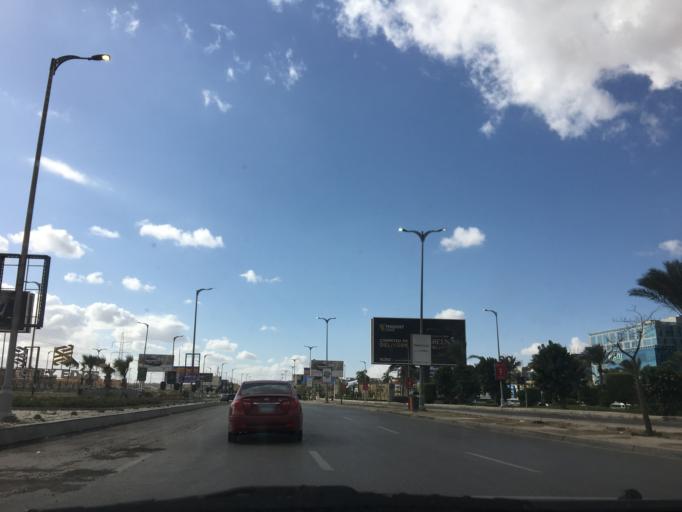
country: EG
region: Al Jizah
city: Awsim
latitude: 30.0244
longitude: 31.0157
